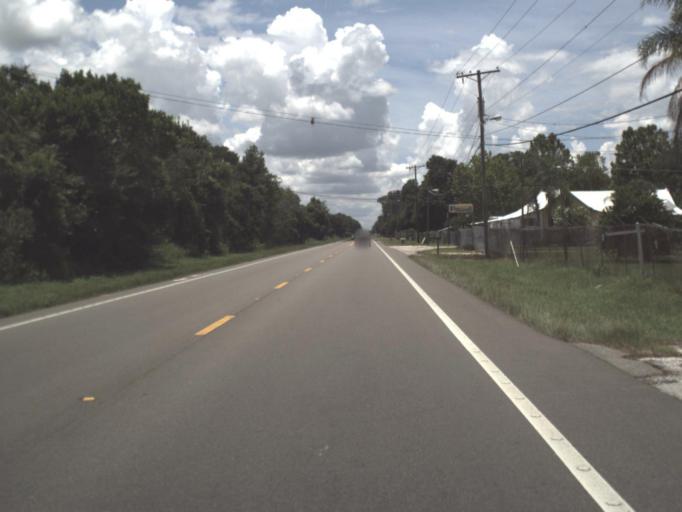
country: US
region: Florida
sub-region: Hillsborough County
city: Plant City
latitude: 28.0236
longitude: -82.0773
